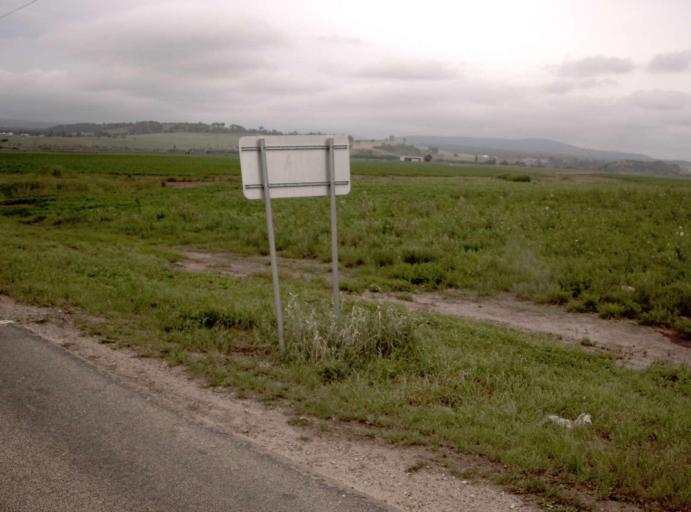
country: AU
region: Victoria
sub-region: East Gippsland
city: Bairnsdale
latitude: -37.7959
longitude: 147.4404
